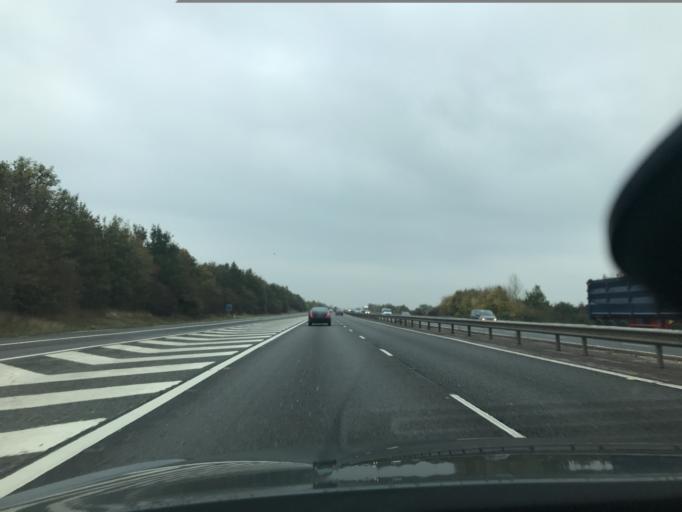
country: GB
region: England
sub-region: Oxfordshire
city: Bicester
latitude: 51.8646
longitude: -1.1925
